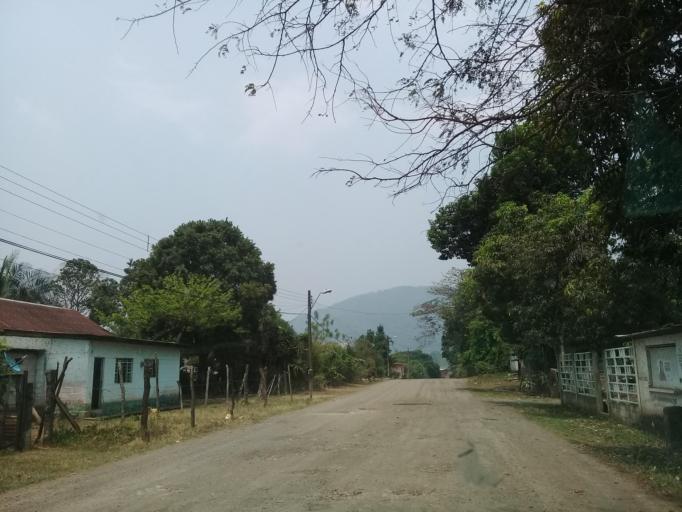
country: MX
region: Veracruz
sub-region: Tezonapa
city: Laguna Chica (Pueblo Nuevo)
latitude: 18.5464
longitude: -96.7331
